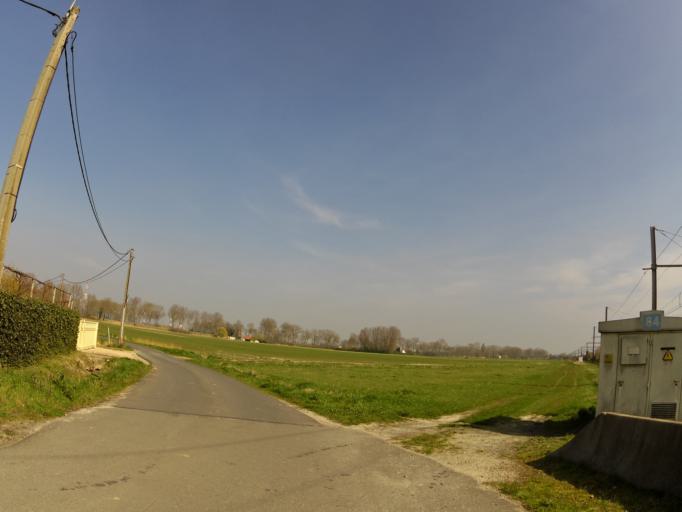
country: BE
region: Flanders
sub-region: Provincie West-Vlaanderen
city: Oudenburg
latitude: 51.2034
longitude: 3.0206
